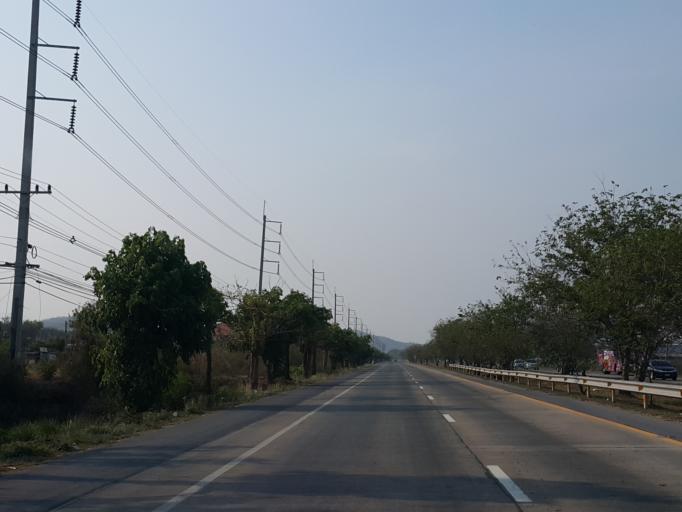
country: TH
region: Suphan Buri
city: Doembang Nangbuat
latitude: 14.8186
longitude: 100.1158
